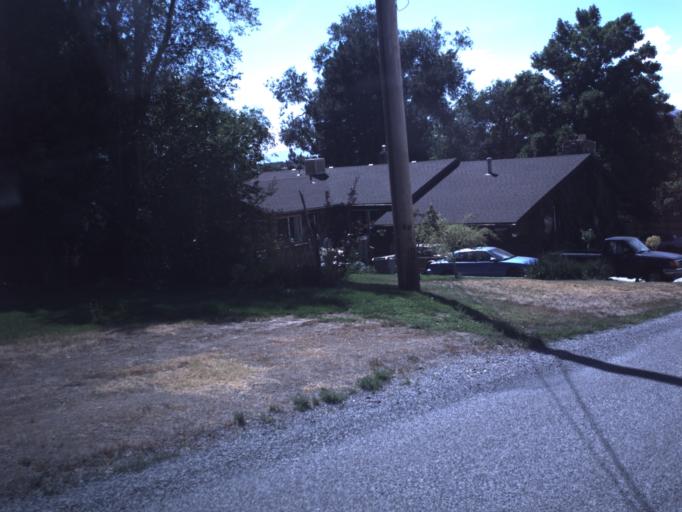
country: US
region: Utah
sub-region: Box Elder County
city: Honeyville
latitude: 41.6347
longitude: -112.0770
